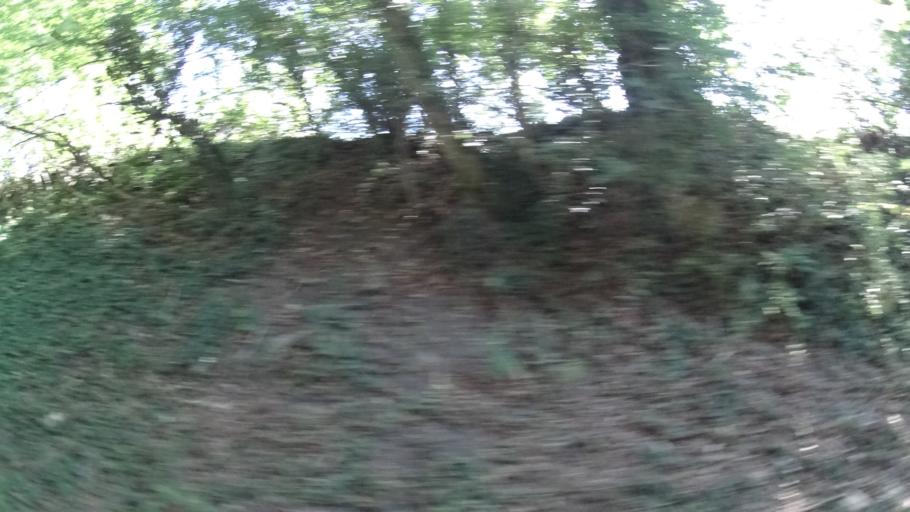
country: DE
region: Baden-Wuerttemberg
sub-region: Karlsruhe Region
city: Bruchsal
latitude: 49.1130
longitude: 8.6437
